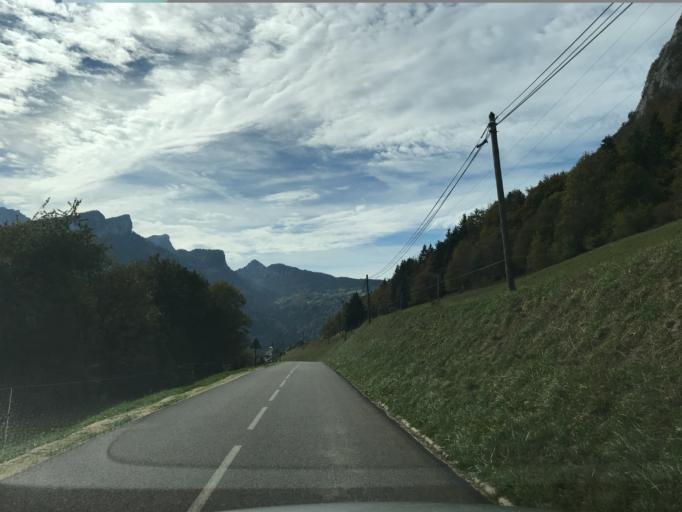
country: FR
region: Rhone-Alpes
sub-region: Departement de la Savoie
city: Les Echelles
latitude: 45.4344
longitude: 5.8290
